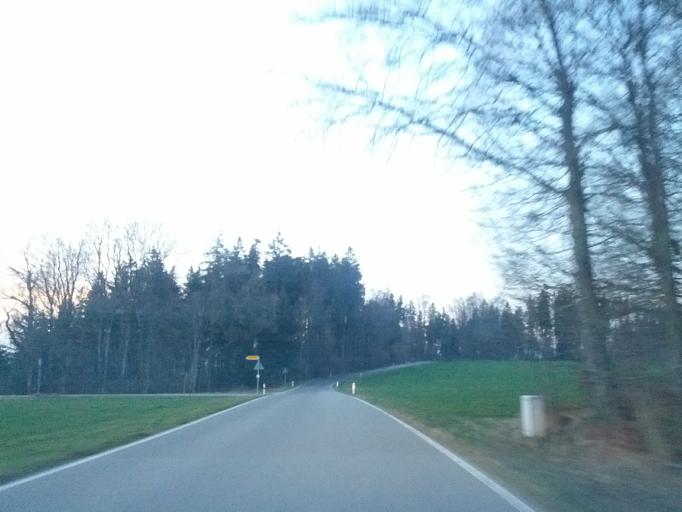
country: DE
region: Baden-Wuerttemberg
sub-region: Tuebingen Region
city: Rot an der Rot
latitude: 47.9427
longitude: 9.9943
